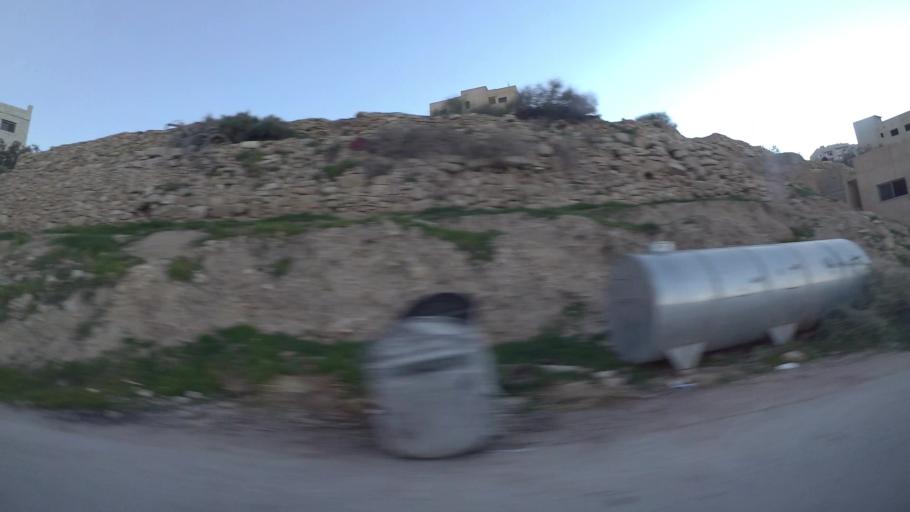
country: JO
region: Ma'an
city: Petra
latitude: 30.3201
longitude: 35.4758
